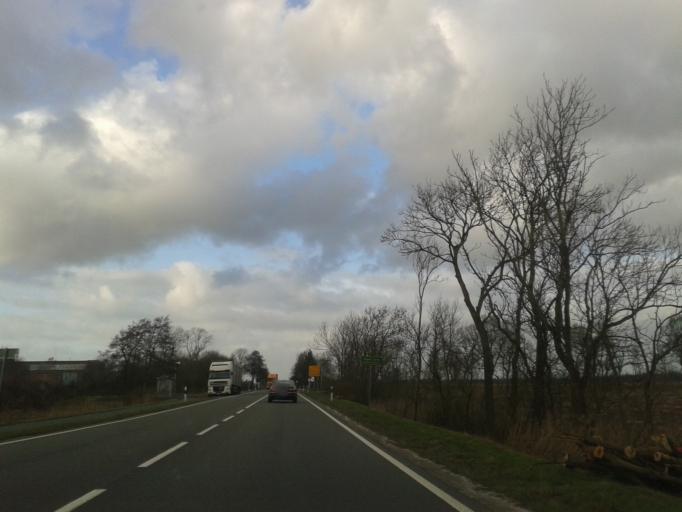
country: DE
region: Lower Saxony
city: Upgant-Schott
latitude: 53.4951
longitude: 7.3044
